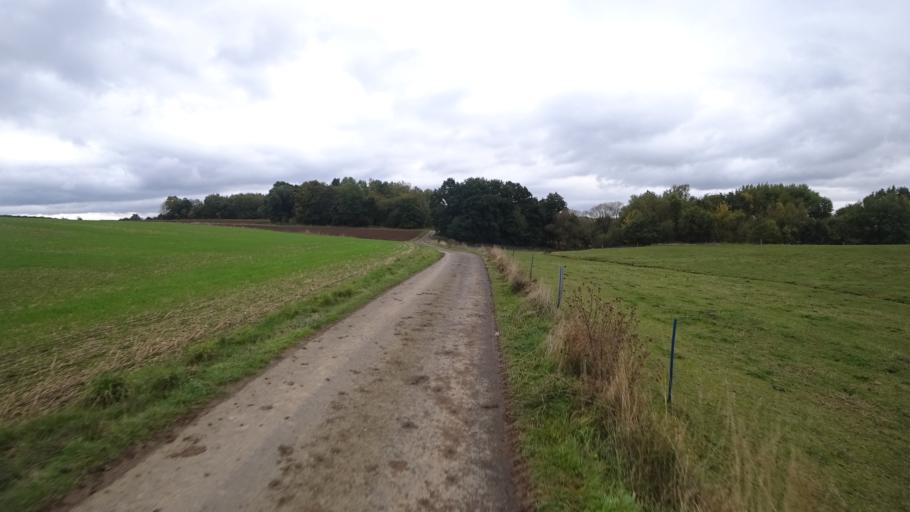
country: DE
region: Rheinland-Pfalz
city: Maxsain
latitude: 50.5539
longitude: 7.7781
